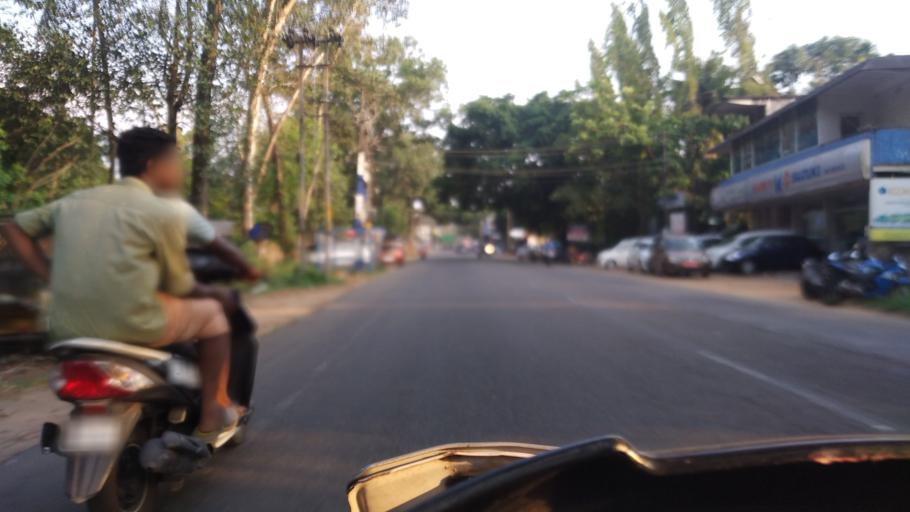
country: IN
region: Kerala
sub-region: Thrissur District
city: Irinjalakuda
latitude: 10.3256
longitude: 76.1434
